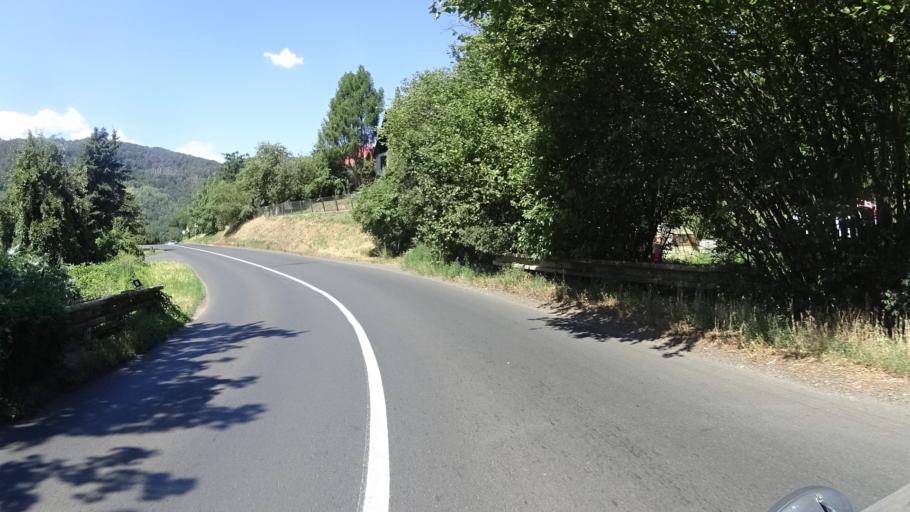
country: CZ
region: Ustecky
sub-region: Okres Usti nad Labem
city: Usti nad Labem
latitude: 50.6278
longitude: 14.0673
